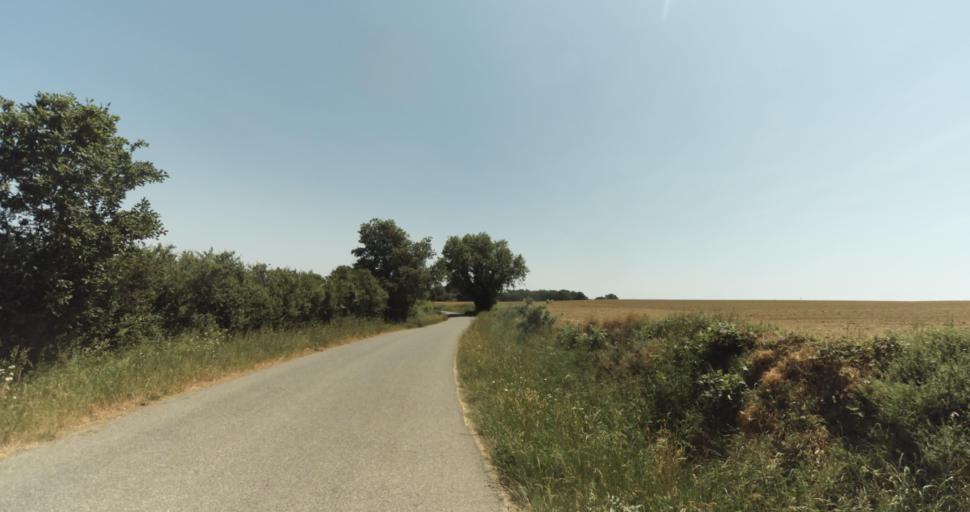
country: FR
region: Midi-Pyrenees
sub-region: Departement de la Haute-Garonne
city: Levignac
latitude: 43.6509
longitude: 1.1964
